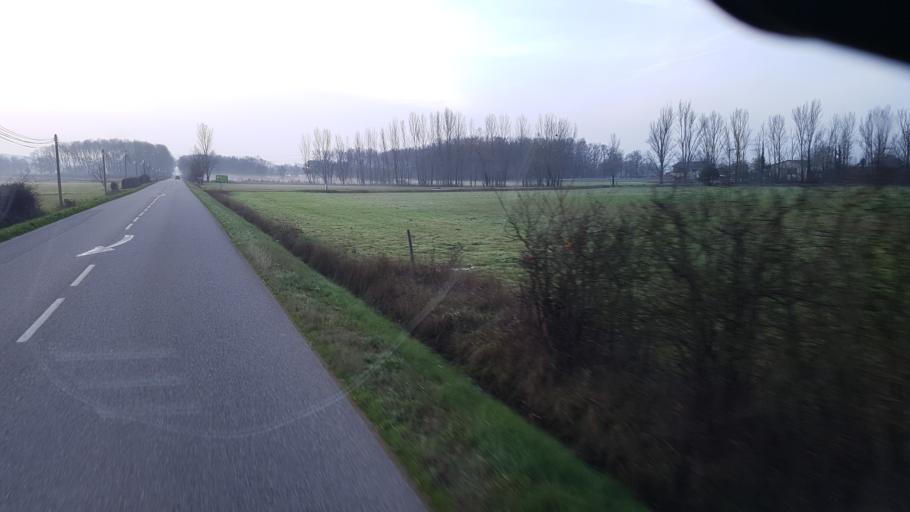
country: FR
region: Midi-Pyrenees
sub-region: Departement du Tarn-et-Garonne
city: Montricoux
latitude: 44.0974
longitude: 1.6033
